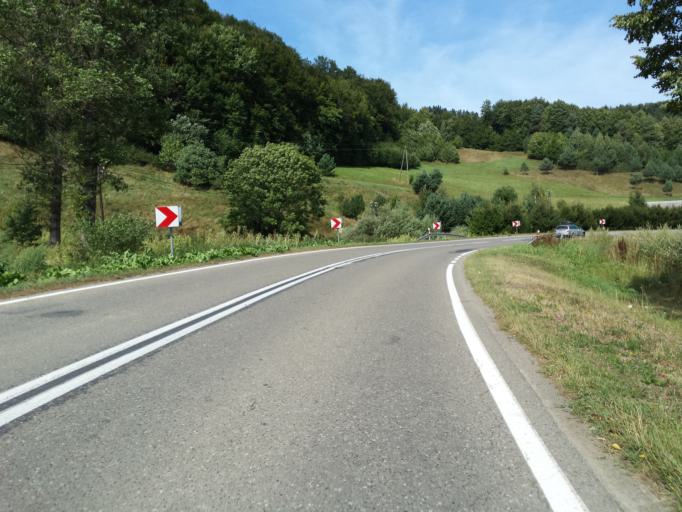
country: PL
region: Subcarpathian Voivodeship
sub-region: Powiat leski
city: Baligrod
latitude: 49.3962
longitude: 22.2797
